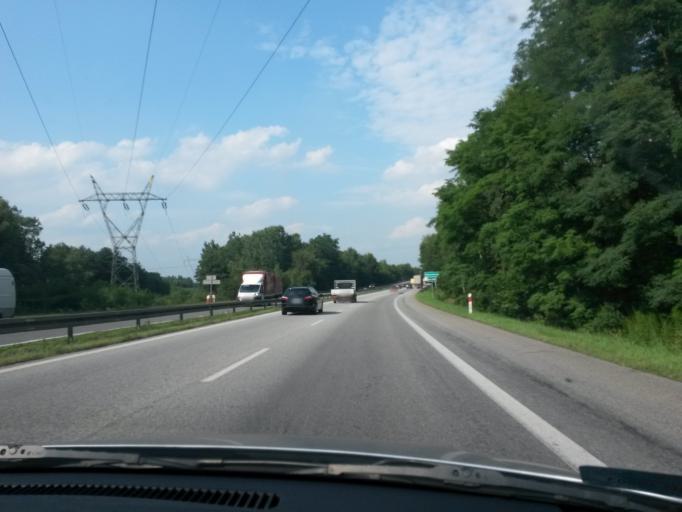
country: PL
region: Silesian Voivodeship
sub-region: Dabrowa Gornicza
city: Dabrowa Gornicza
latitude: 50.3069
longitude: 19.2262
